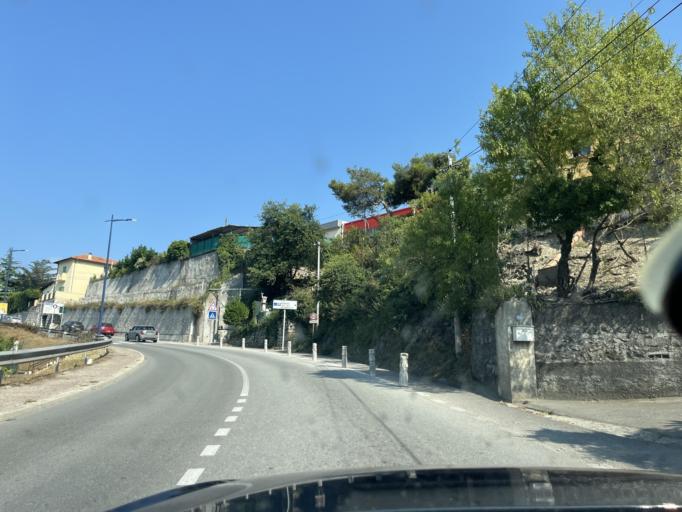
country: FR
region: Provence-Alpes-Cote d'Azur
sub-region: Departement des Alpes-Maritimes
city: La Turbie
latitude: 43.7443
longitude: 7.3923
